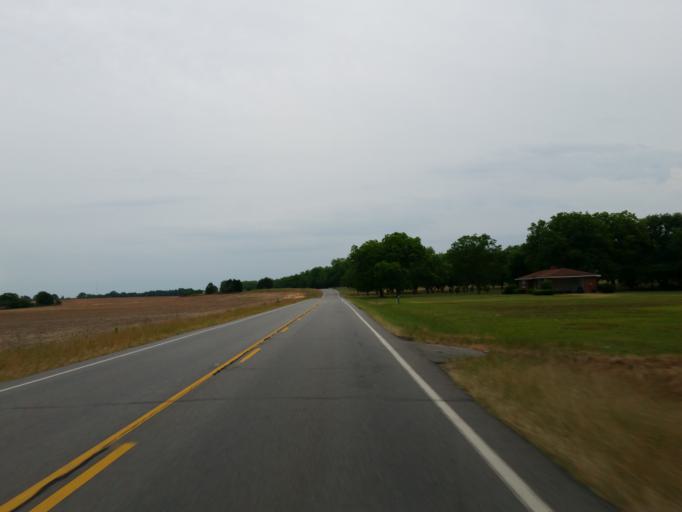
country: US
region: Georgia
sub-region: Dooly County
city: Unadilla
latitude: 32.2227
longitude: -83.7580
